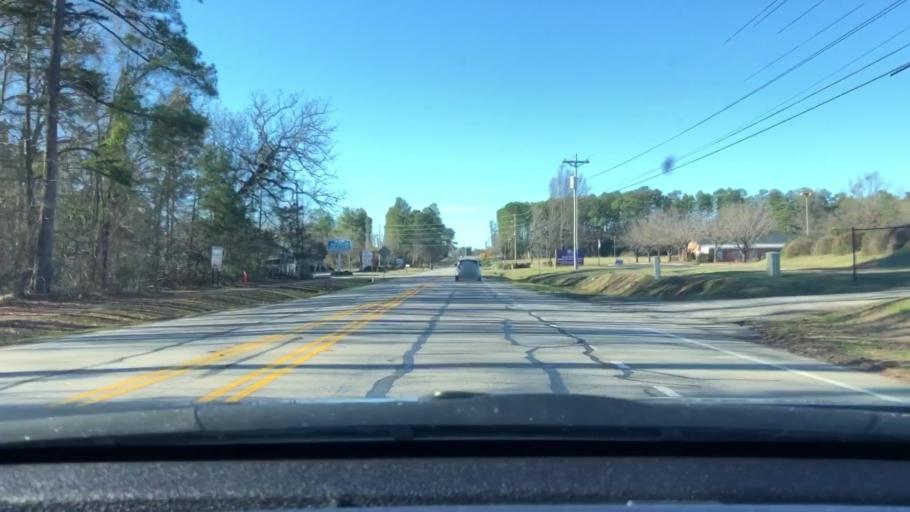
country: US
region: South Carolina
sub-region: Lexington County
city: Irmo
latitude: 34.1023
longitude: -81.1820
